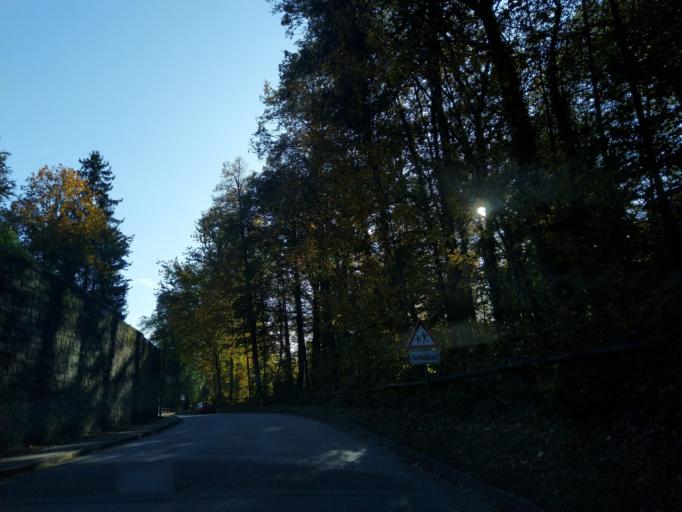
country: DE
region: Bavaria
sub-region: Lower Bavaria
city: Metten
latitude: 48.8821
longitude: 12.9230
